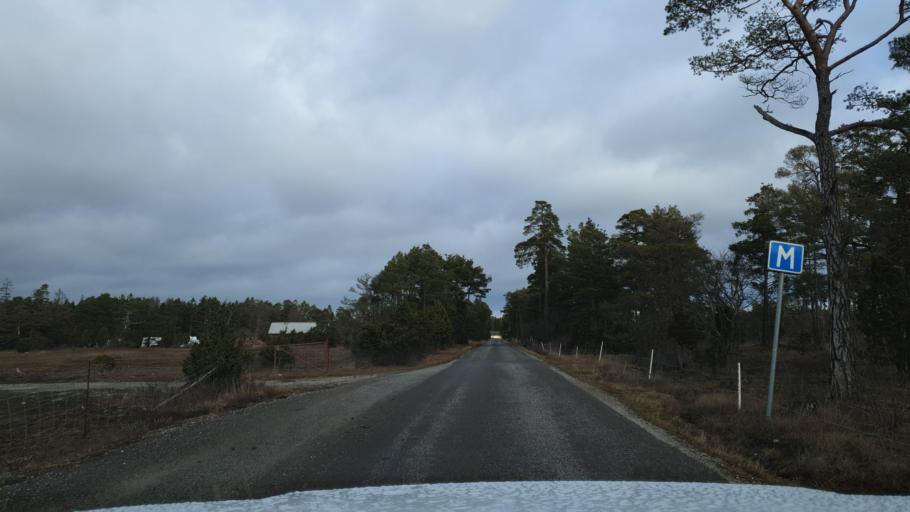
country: SE
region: Gotland
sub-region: Gotland
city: Slite
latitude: 57.3797
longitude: 18.8049
